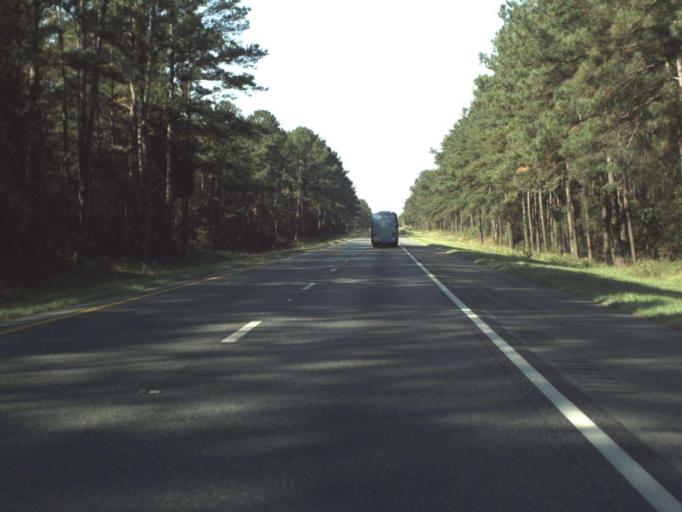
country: US
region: Florida
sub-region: Walton County
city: DeFuniak Springs
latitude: 30.6972
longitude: -85.9899
